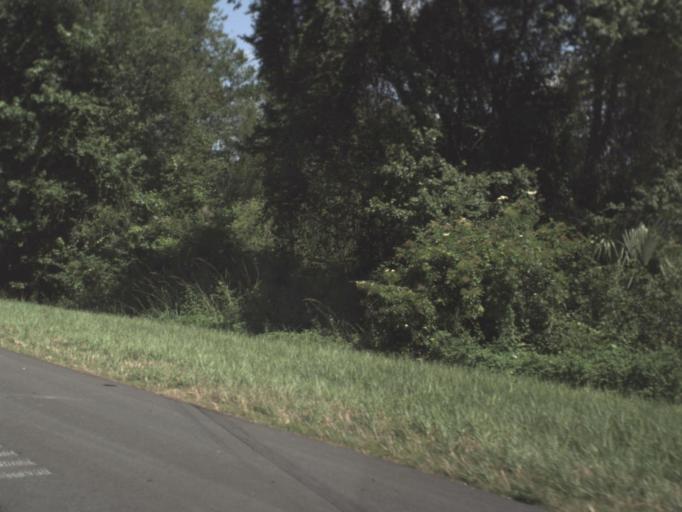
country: US
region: Florida
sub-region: Madison County
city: Madison
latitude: 30.4081
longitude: -83.4091
